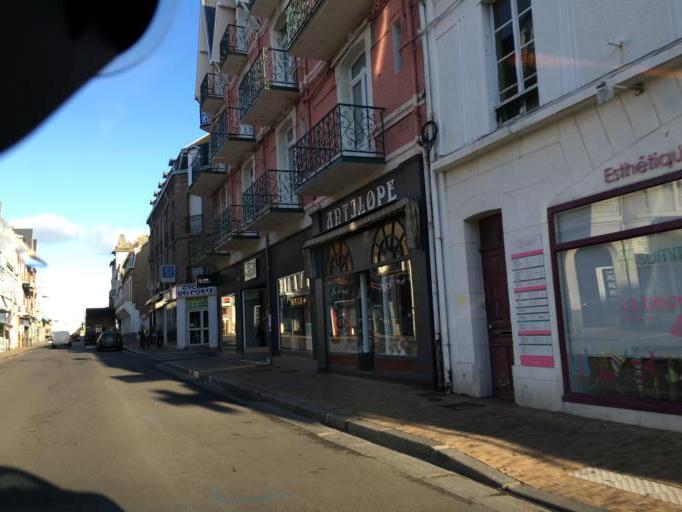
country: FR
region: Nord-Pas-de-Calais
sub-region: Departement du Pas-de-Calais
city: Berck-Plage
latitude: 50.4047
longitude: 1.5651
